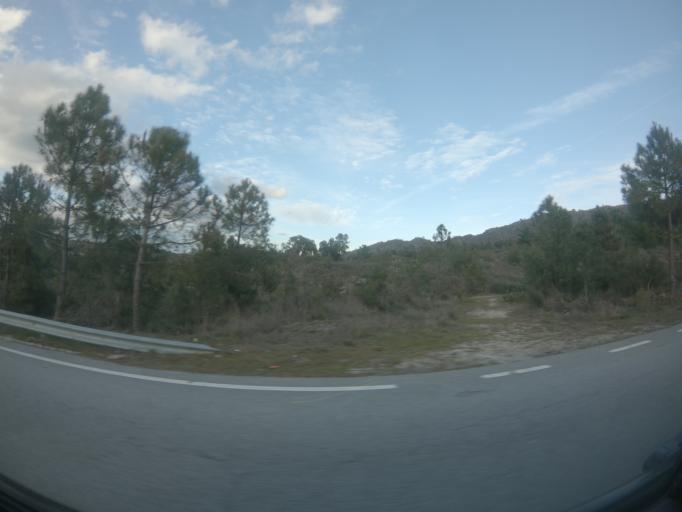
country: PT
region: Braganca
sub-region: Carrazeda de Ansiaes
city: Carrazeda de Anciaes
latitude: 41.2928
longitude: -7.3385
